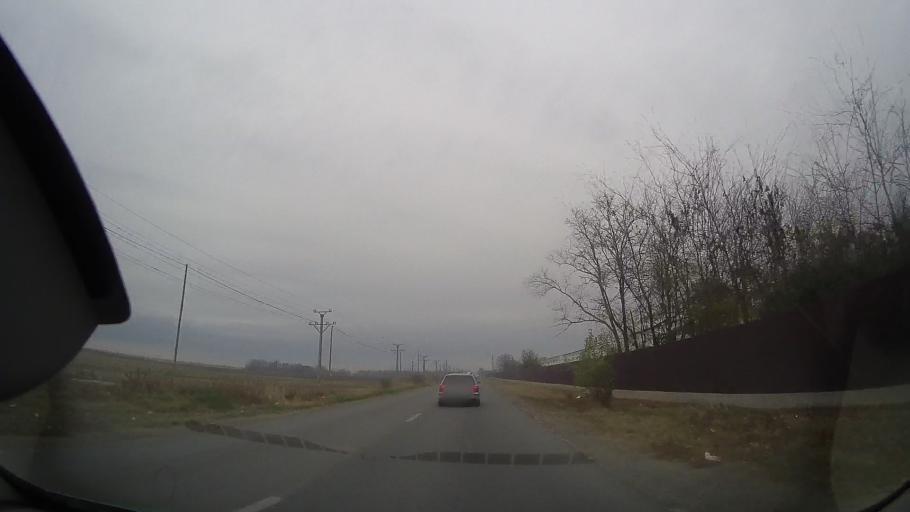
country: RO
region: Ialomita
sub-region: Oras Amara
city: Amara
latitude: 44.5870
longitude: 27.3325
